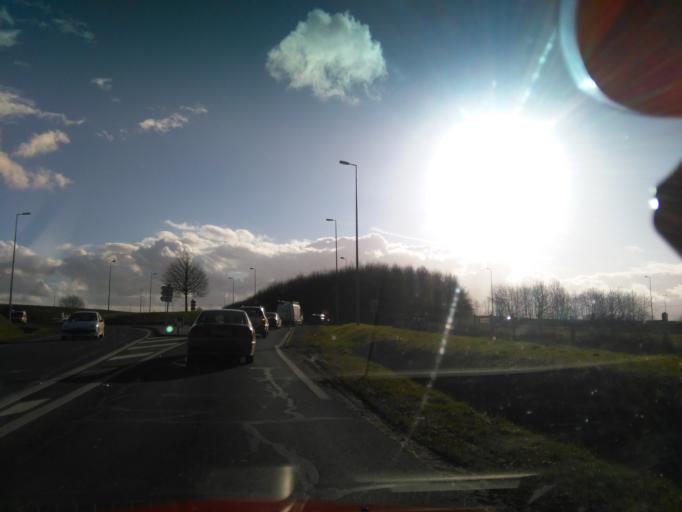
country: FR
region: Lower Normandy
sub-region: Departement du Calvados
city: Bretteville-sur-Odon
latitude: 49.1542
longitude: -0.4159
